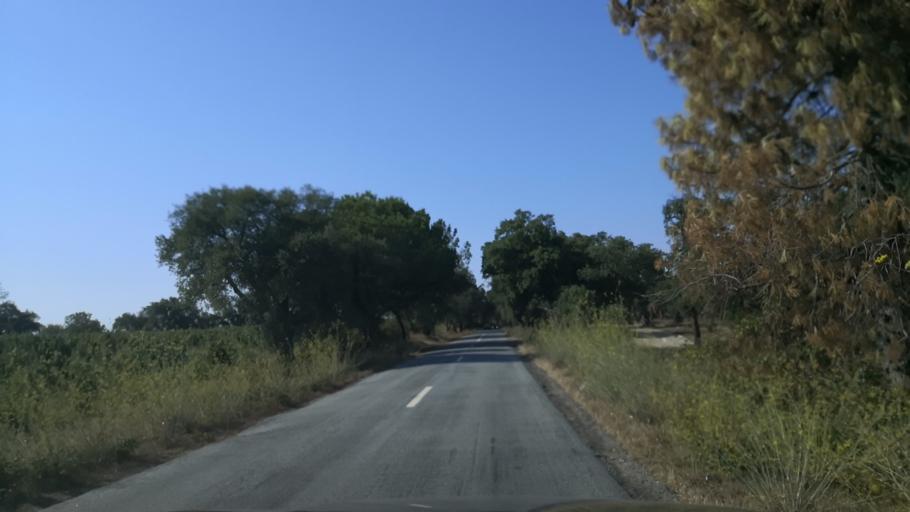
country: PT
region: Santarem
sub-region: Benavente
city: Poceirao
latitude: 38.7469
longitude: -8.6308
